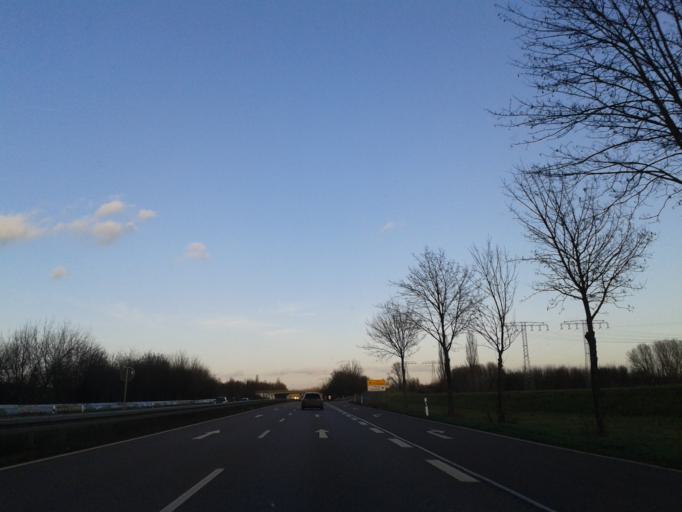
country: DE
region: Saxony-Anhalt
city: Halle Neustadt
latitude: 51.4705
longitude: 11.9349
